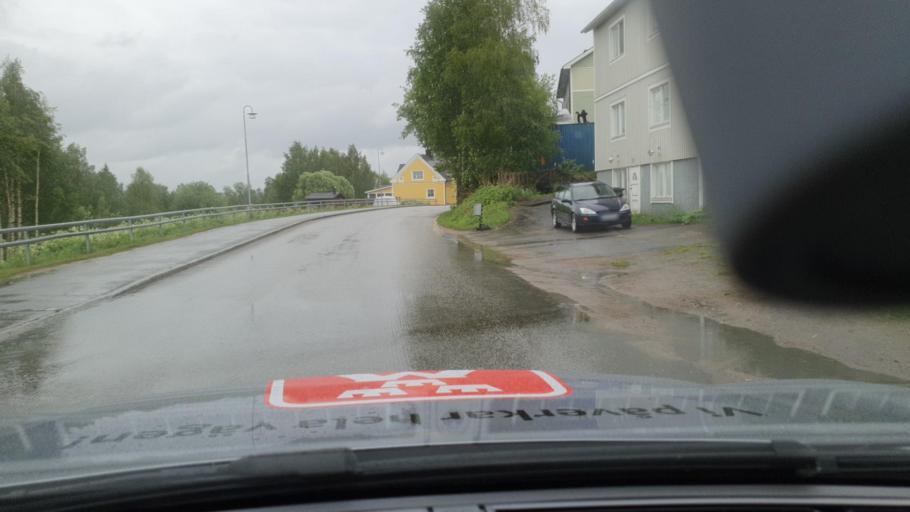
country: SE
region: Norrbotten
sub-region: Overtornea Kommun
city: OEvertornea
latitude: 66.3942
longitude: 23.6527
